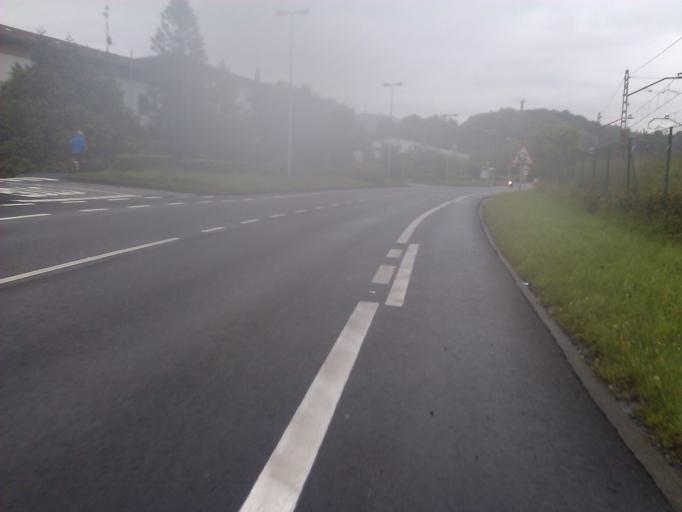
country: ES
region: Basque Country
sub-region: Provincia de Guipuzcoa
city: San Sebastian
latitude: 43.3032
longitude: -1.9591
